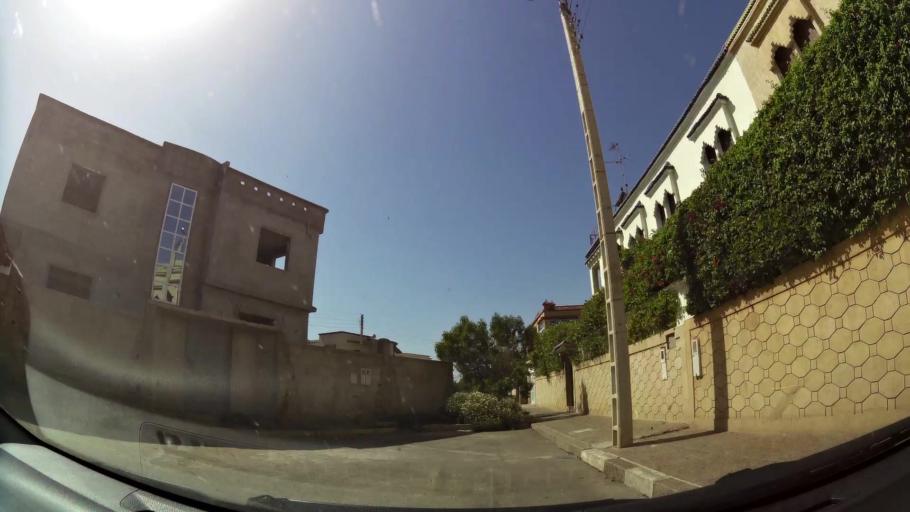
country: MA
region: Souss-Massa-Draa
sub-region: Inezgane-Ait Mellou
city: Inezgane
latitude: 30.3769
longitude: -9.5598
